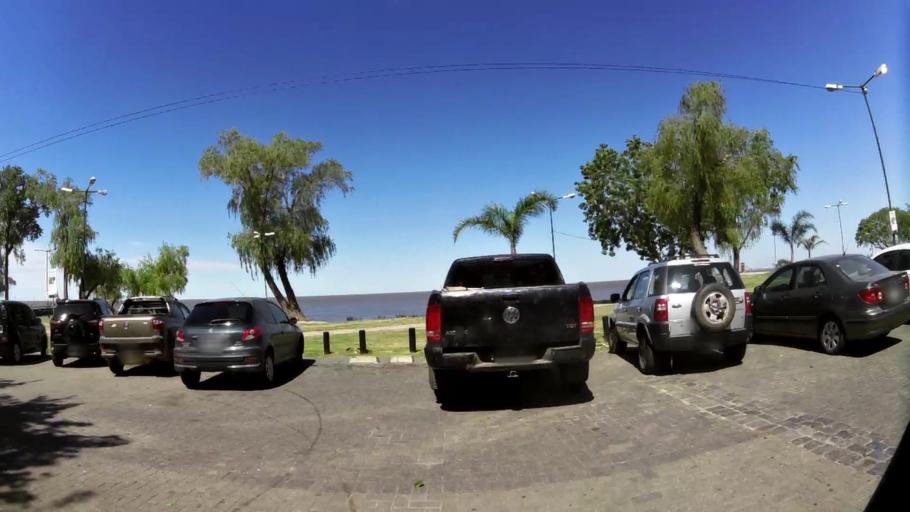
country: AR
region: Buenos Aires
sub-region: Partido de Vicente Lopez
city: Olivos
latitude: -34.4858
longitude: -58.4812
